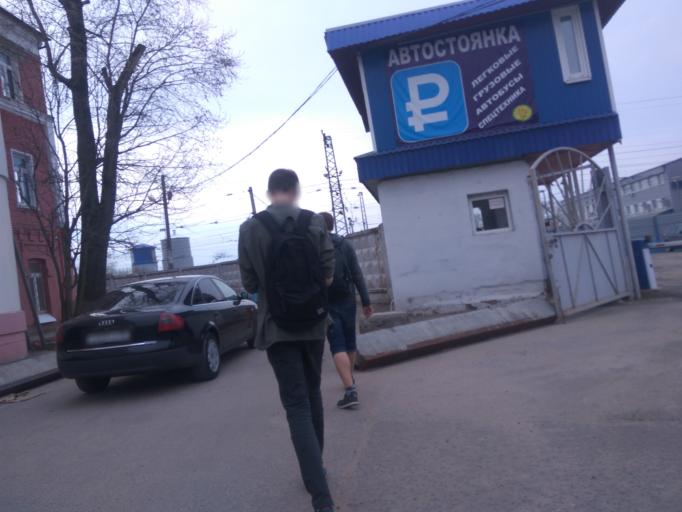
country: RU
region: Vladimir
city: Aleksandrov
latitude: 56.4000
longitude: 38.7084
